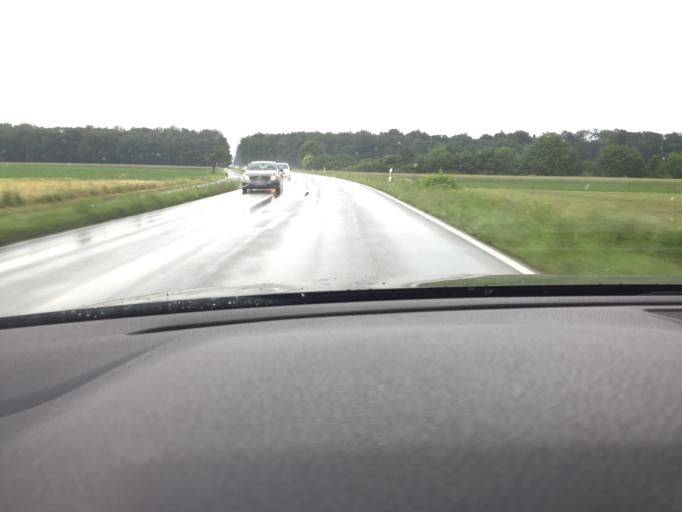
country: DE
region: Hesse
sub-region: Regierungsbezirk Darmstadt
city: Rodgau
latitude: 50.0192
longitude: 8.9264
